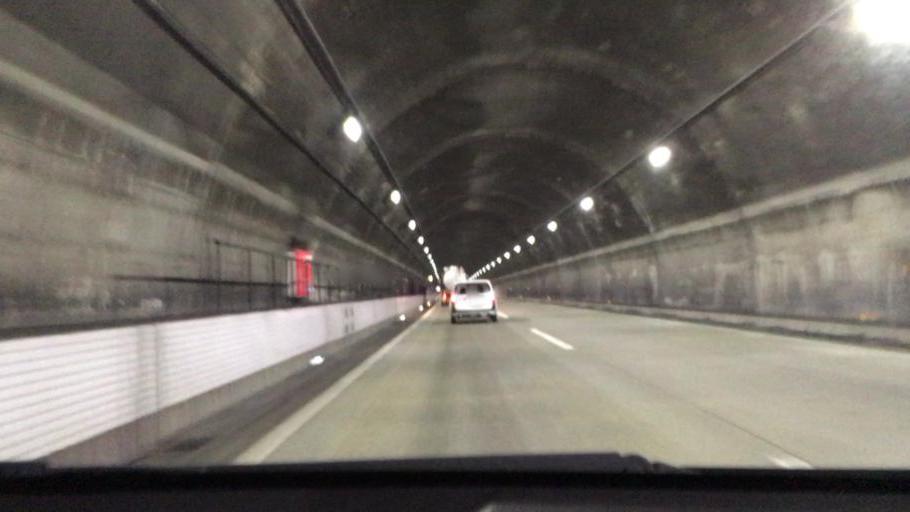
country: JP
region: Yamaguchi
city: Tokuyama
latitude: 34.0733
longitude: 131.7125
